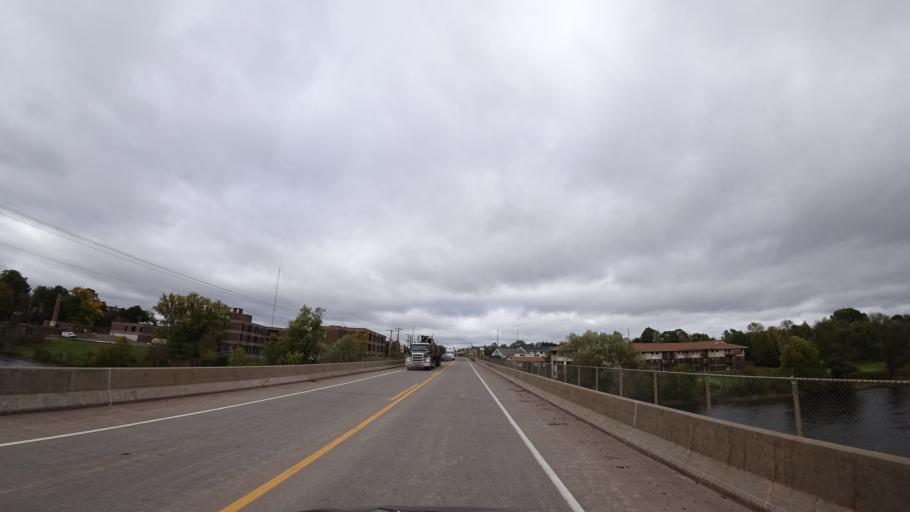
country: US
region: Wisconsin
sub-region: Rusk County
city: Ladysmith
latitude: 45.4532
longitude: -91.1093
